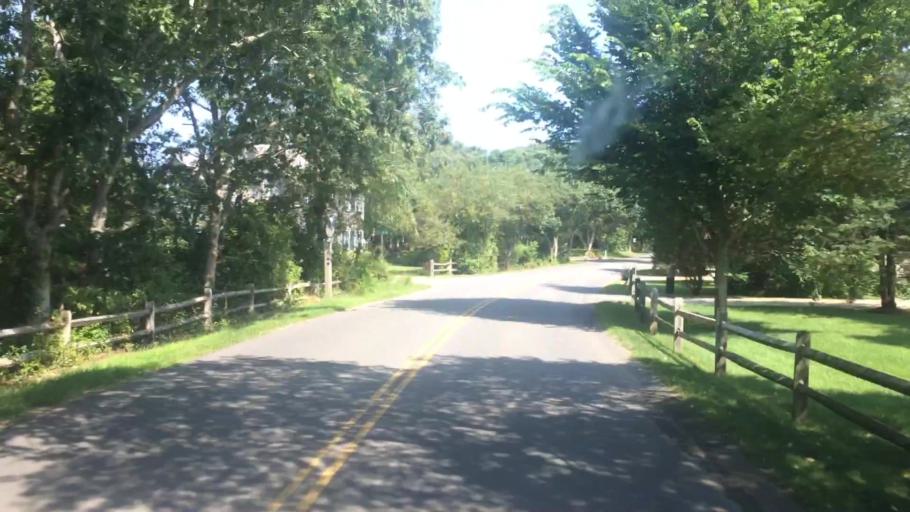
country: US
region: Massachusetts
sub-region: Dukes County
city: Edgartown
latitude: 41.3773
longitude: -70.5284
